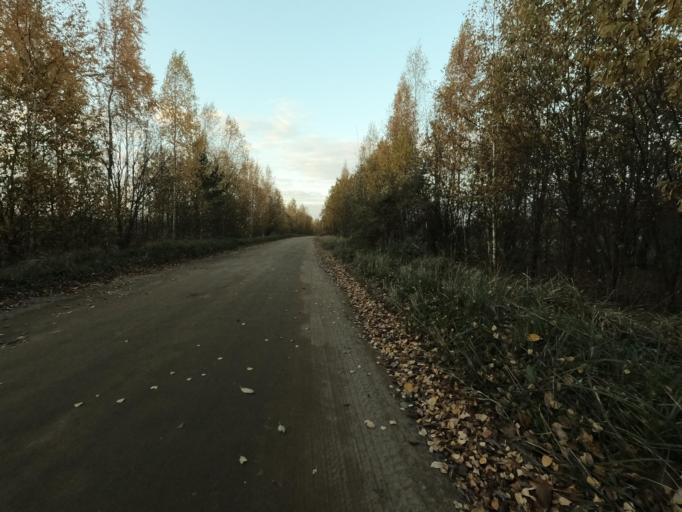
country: RU
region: Leningrad
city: Mga
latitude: 59.7967
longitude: 31.2002
